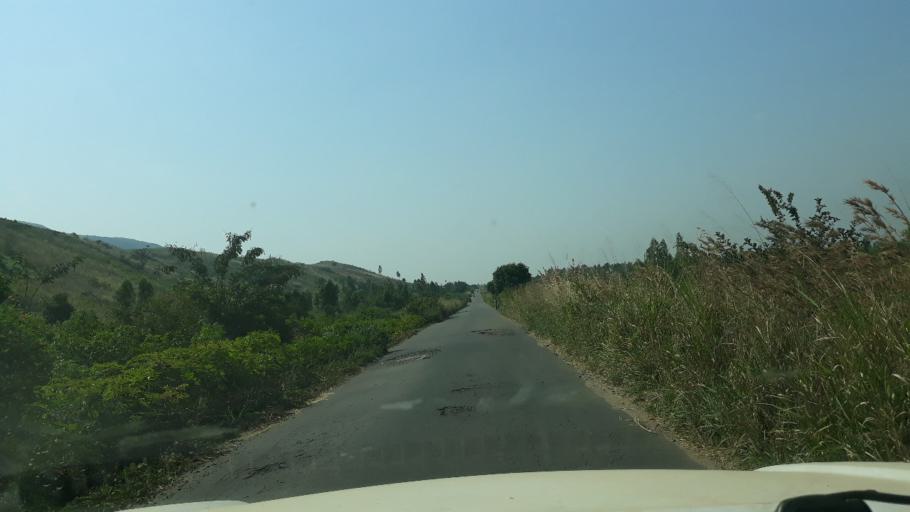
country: CD
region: South Kivu
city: Uvira
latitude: -3.2740
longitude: 29.1610
